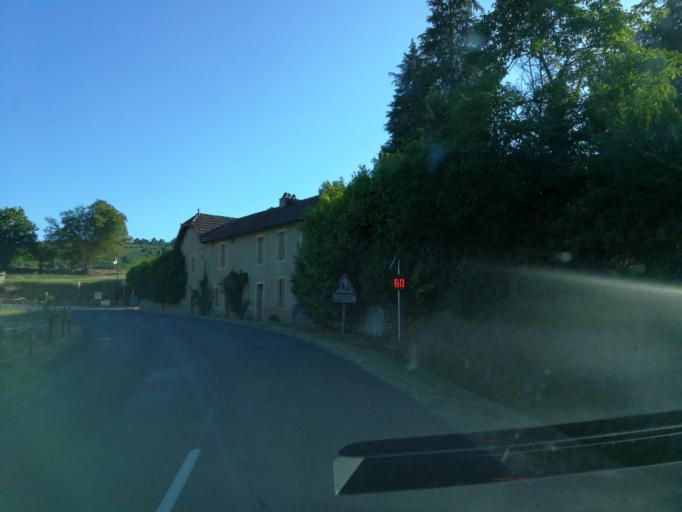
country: FR
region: Midi-Pyrenees
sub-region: Departement du Lot
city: Salviac
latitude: 44.6210
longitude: 1.2103
